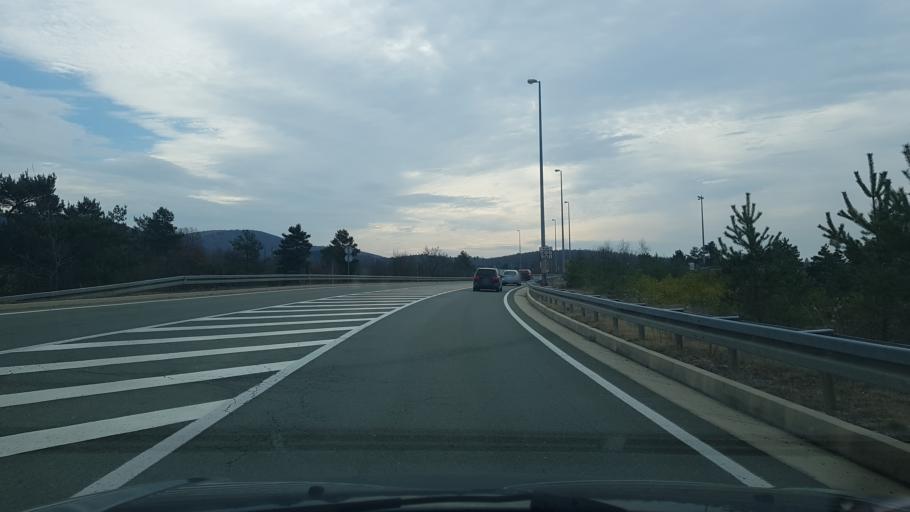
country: HR
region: Primorsko-Goranska
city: Klana
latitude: 45.4756
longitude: 14.2723
